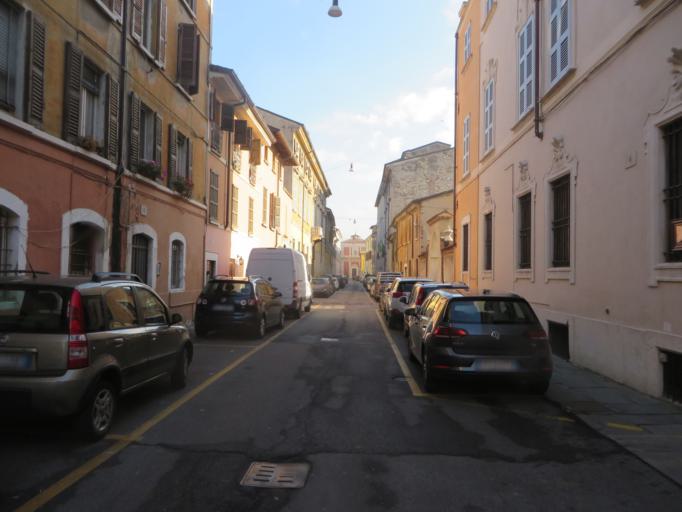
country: IT
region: Lombardy
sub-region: Provincia di Brescia
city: Brescia
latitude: 45.5334
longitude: 10.2256
